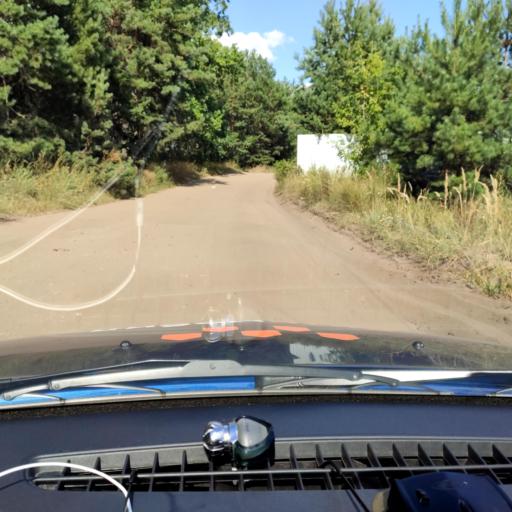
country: RU
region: Voronezj
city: Somovo
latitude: 51.7166
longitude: 39.3777
